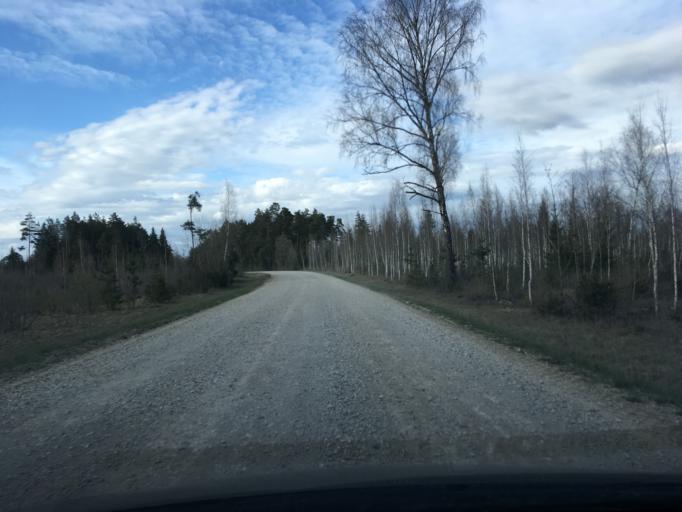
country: EE
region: Raplamaa
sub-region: Maerjamaa vald
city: Marjamaa
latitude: 58.9530
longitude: 24.3245
